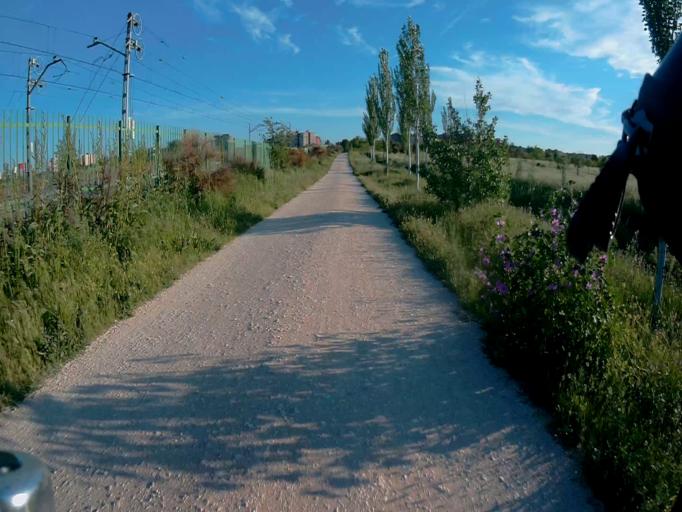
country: ES
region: Madrid
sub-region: Provincia de Madrid
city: Fuenlabrada
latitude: 40.3005
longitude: -3.7906
